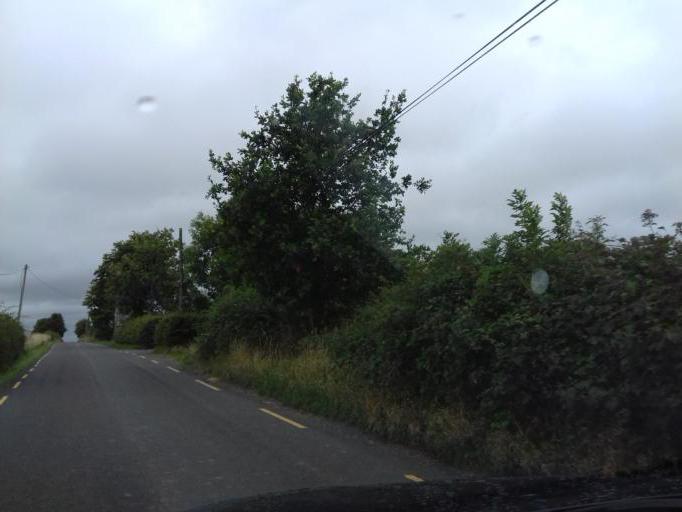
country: IE
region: Leinster
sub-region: County Carlow
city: Bagenalstown
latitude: 52.6181
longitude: -7.0366
